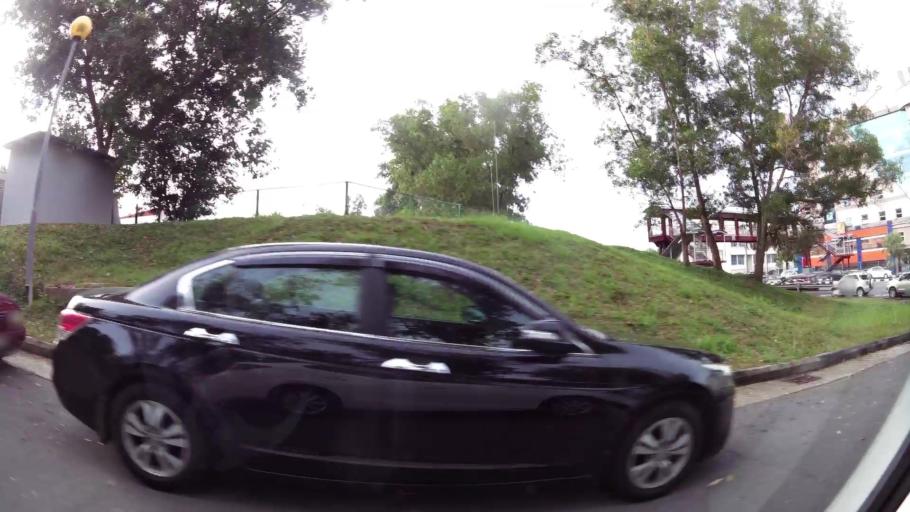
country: BN
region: Brunei and Muara
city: Bandar Seri Begawan
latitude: 4.9000
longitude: 114.9010
